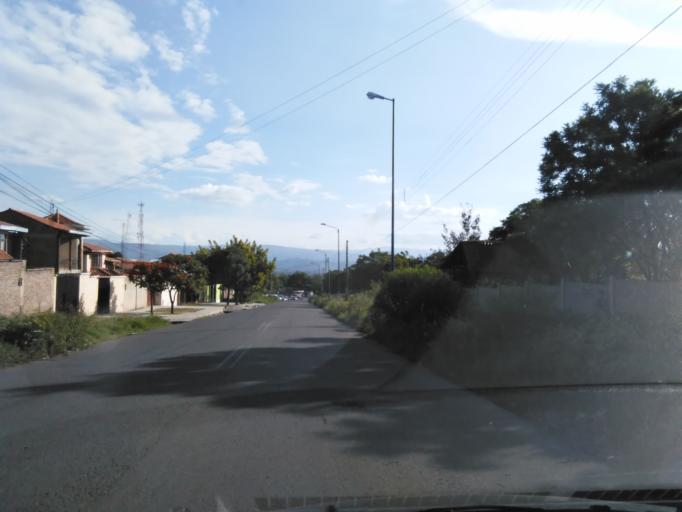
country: BO
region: Cochabamba
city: Cochabamba
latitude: -17.3486
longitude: -66.1833
